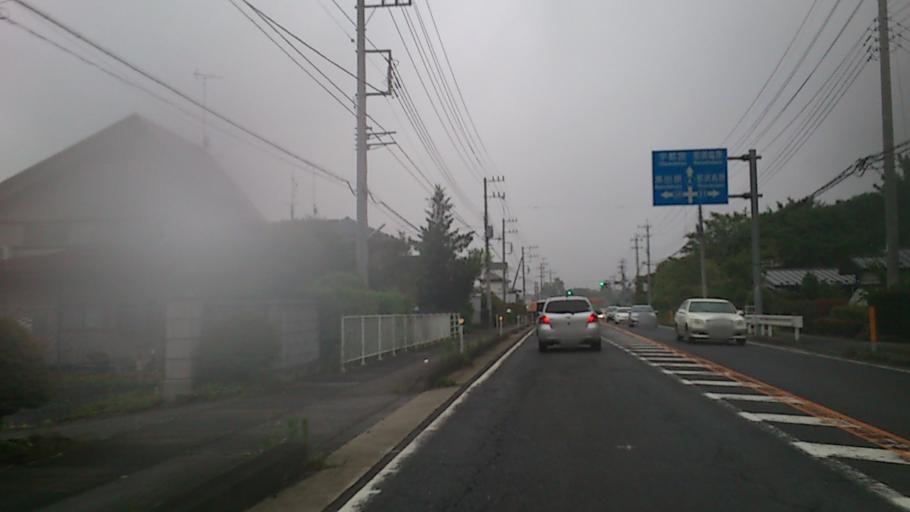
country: JP
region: Tochigi
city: Kuroiso
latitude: 37.0418
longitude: 140.0991
